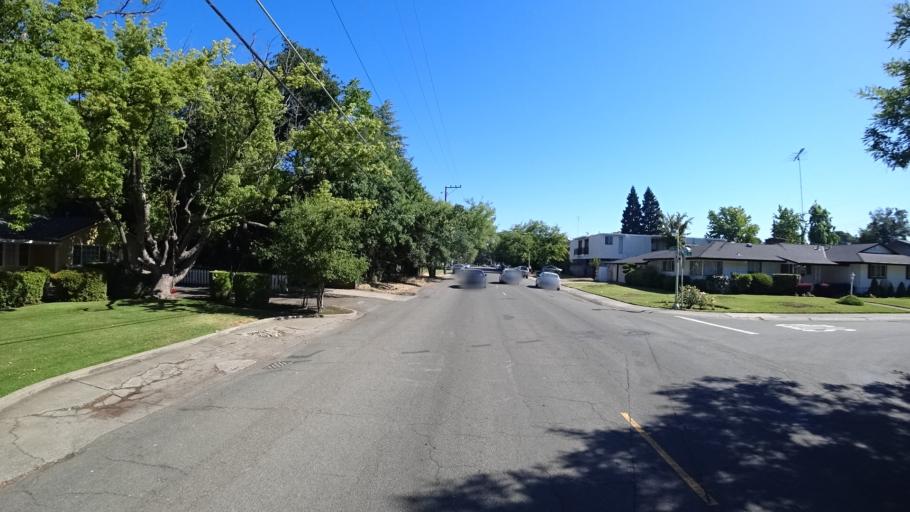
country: US
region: California
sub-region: Sacramento County
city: Sacramento
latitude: 38.5353
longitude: -121.5042
